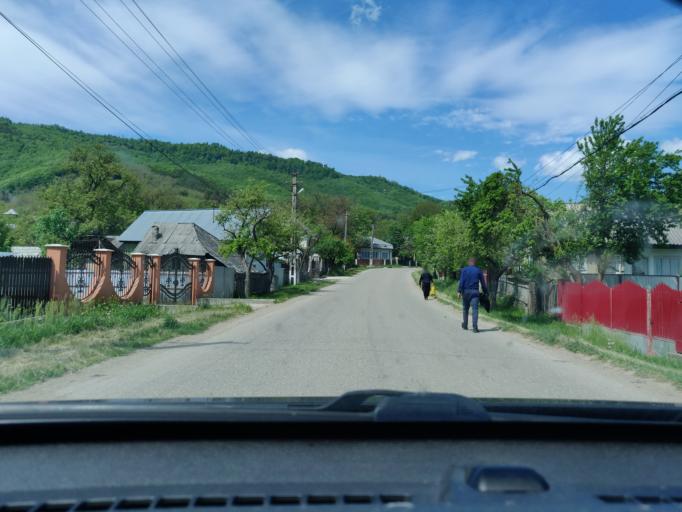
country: RO
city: Vizantea-Manastireasca
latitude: 45.9829
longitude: 26.7844
